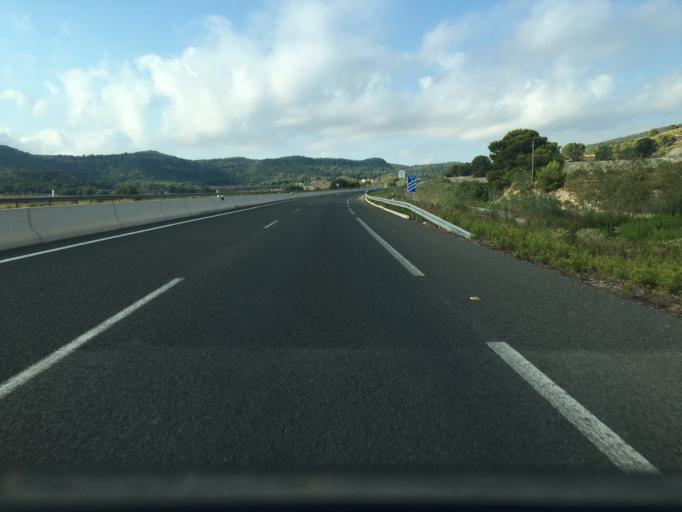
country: ES
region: Murcia
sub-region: Murcia
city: Beniel
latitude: 37.9440
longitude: -0.9532
